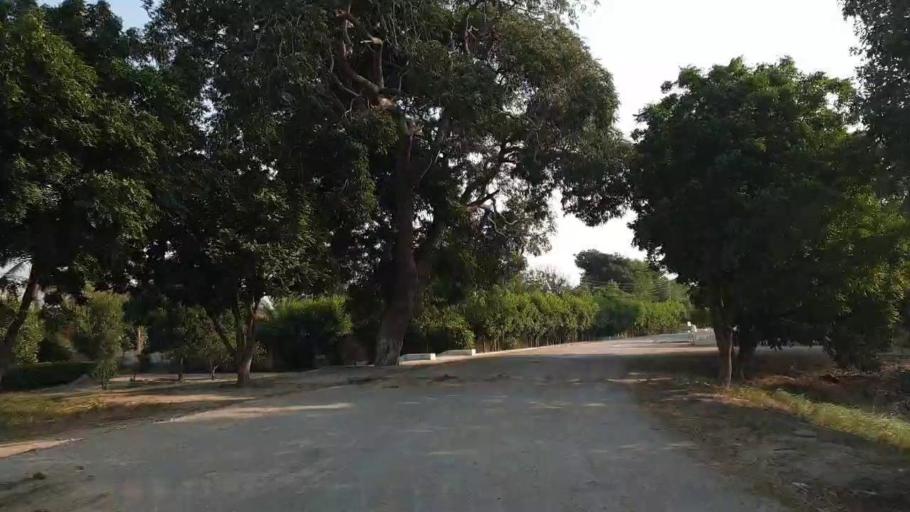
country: PK
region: Sindh
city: Bulri
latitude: 24.9865
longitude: 68.3919
